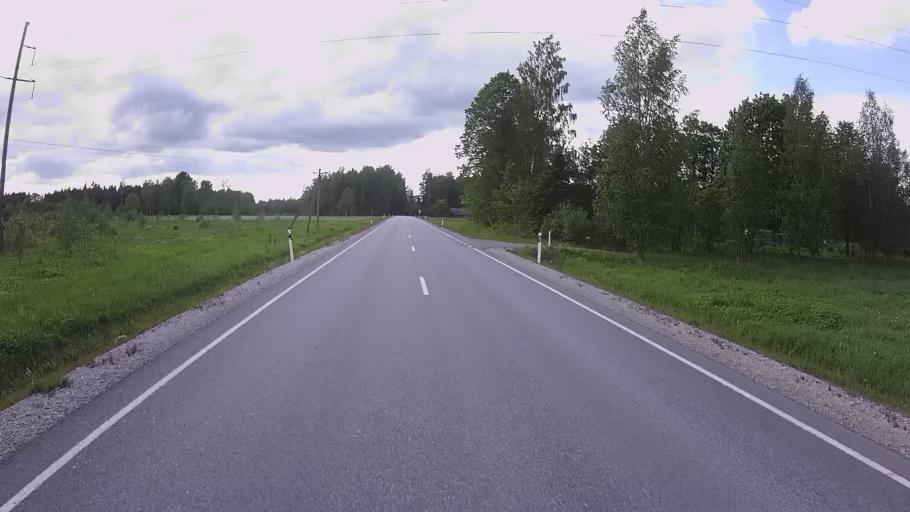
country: EE
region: Jogevamaa
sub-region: Mustvee linn
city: Mustvee
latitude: 58.8684
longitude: 26.8321
